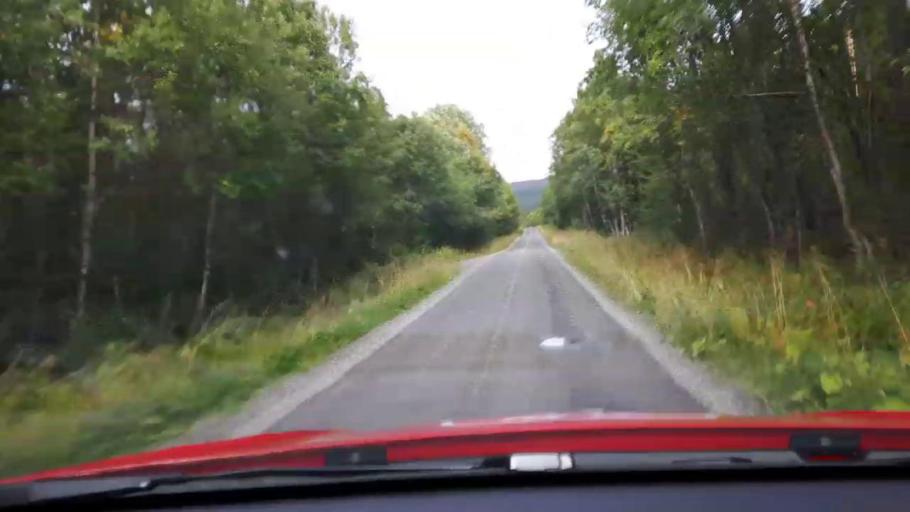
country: SE
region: Jaemtland
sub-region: Are Kommun
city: Are
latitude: 63.8010
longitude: 13.1111
